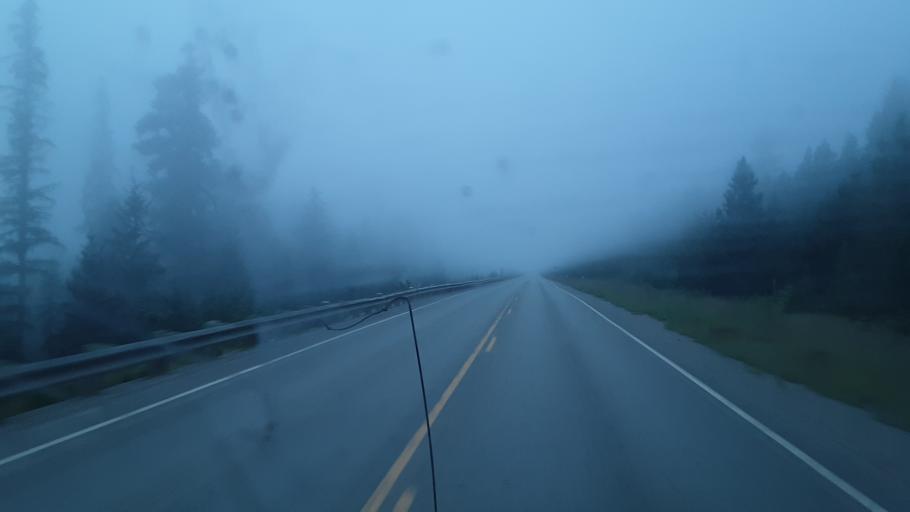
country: US
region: Montana
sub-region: Flathead County
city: Kalispell
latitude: 48.0440
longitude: -114.8521
